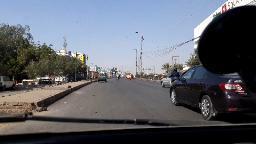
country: PK
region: Sindh
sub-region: Karachi District
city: Karachi
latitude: 24.9008
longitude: 67.1144
